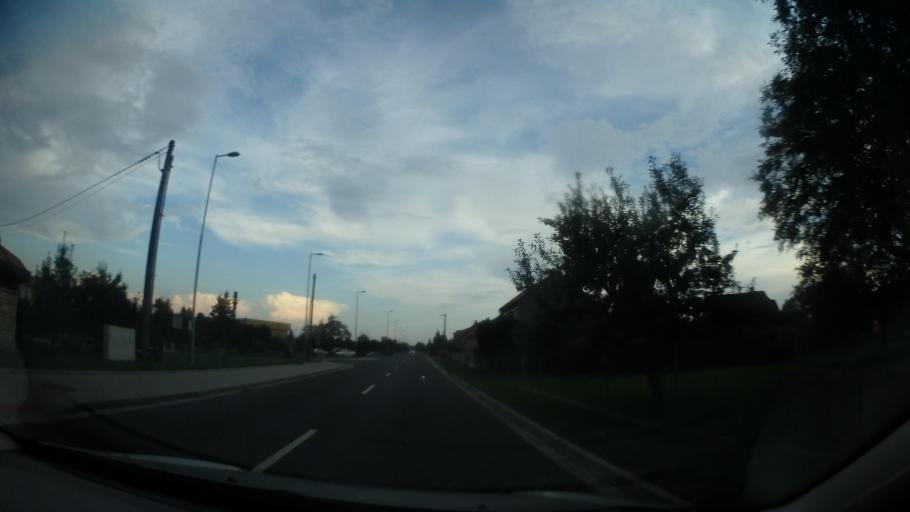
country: CZ
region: Olomoucky
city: Troubky
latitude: 49.4287
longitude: 17.3407
